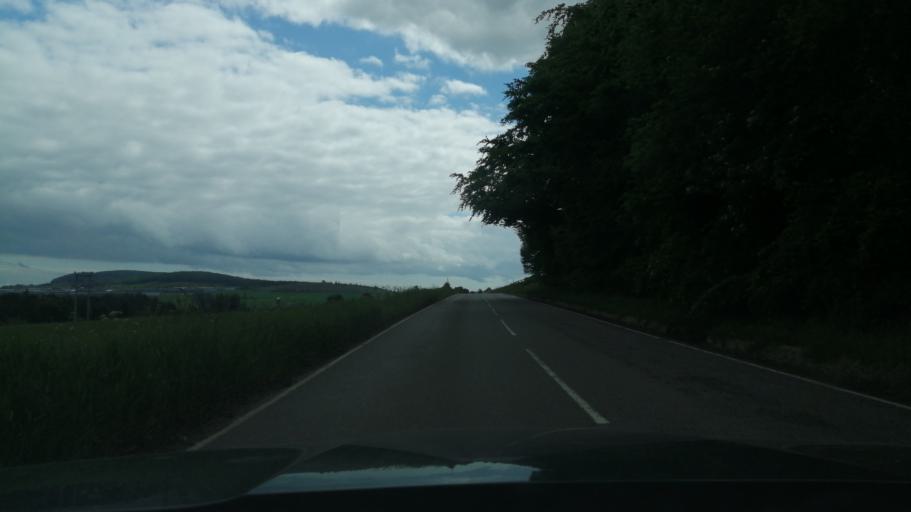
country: GB
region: Scotland
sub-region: Moray
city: Fochabers
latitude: 57.5479
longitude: -3.1069
